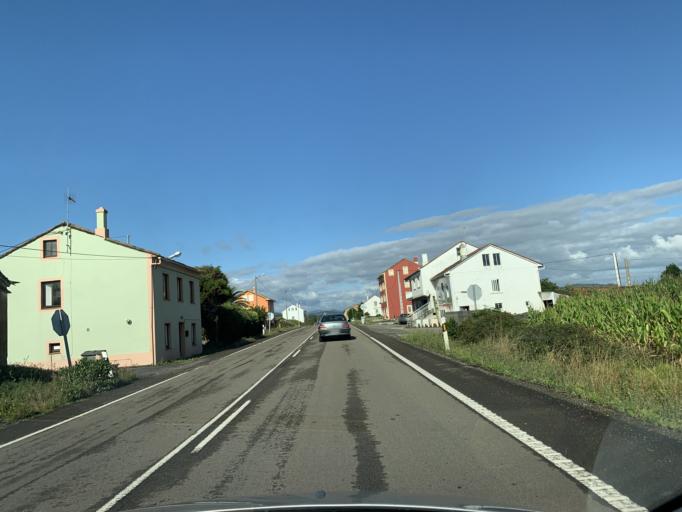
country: ES
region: Galicia
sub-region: Provincia de Lugo
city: Barreiros
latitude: 43.5456
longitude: -7.1981
